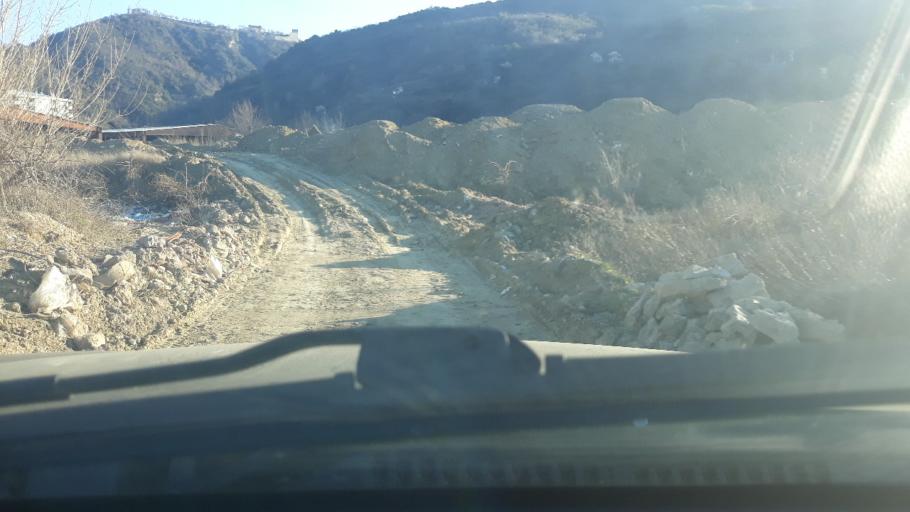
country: MK
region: Strumica
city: Strumica
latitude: 41.4418
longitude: 22.6274
